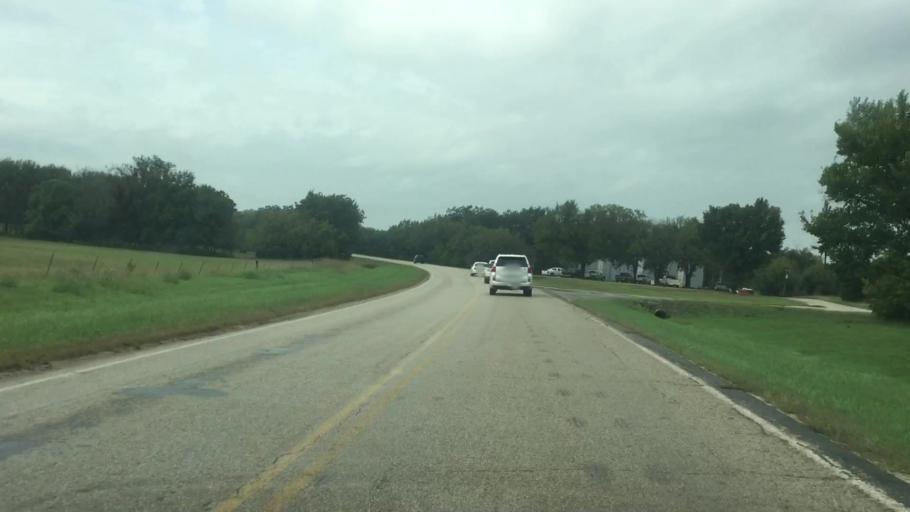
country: US
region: Kansas
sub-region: Allen County
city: Iola
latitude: 37.8855
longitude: -95.4290
